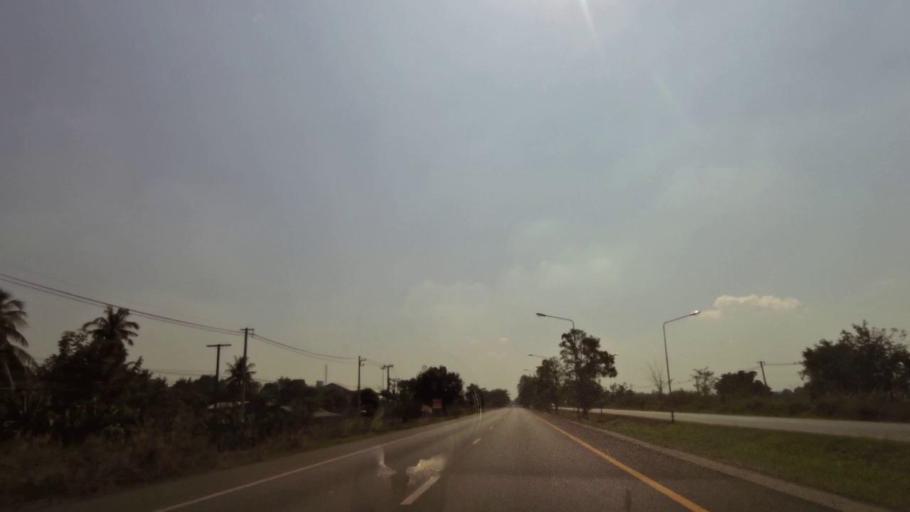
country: TH
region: Phichit
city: Bueng Na Rang
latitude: 16.2585
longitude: 100.1259
